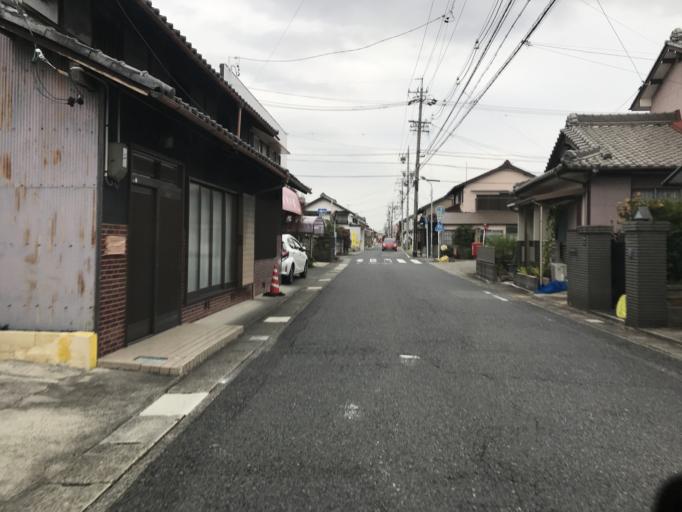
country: JP
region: Aichi
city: Inazawa
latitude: 35.2095
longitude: 136.8399
